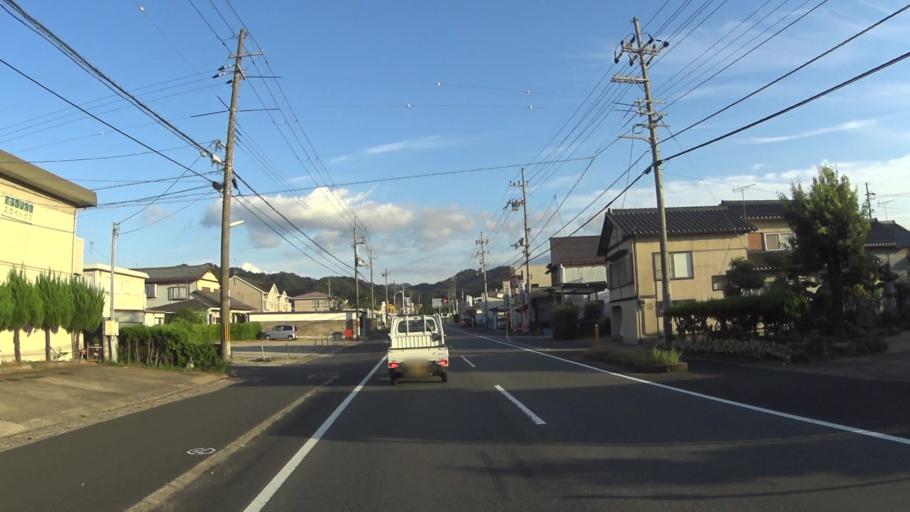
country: JP
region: Kyoto
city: Miyazu
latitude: 35.5856
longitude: 135.0979
